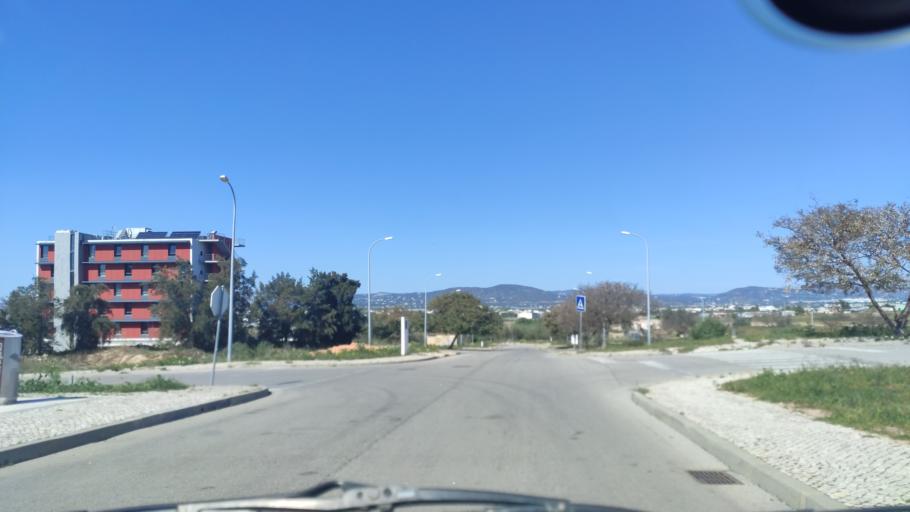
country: PT
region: Faro
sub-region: Faro
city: Faro
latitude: 37.0324
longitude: -7.9365
